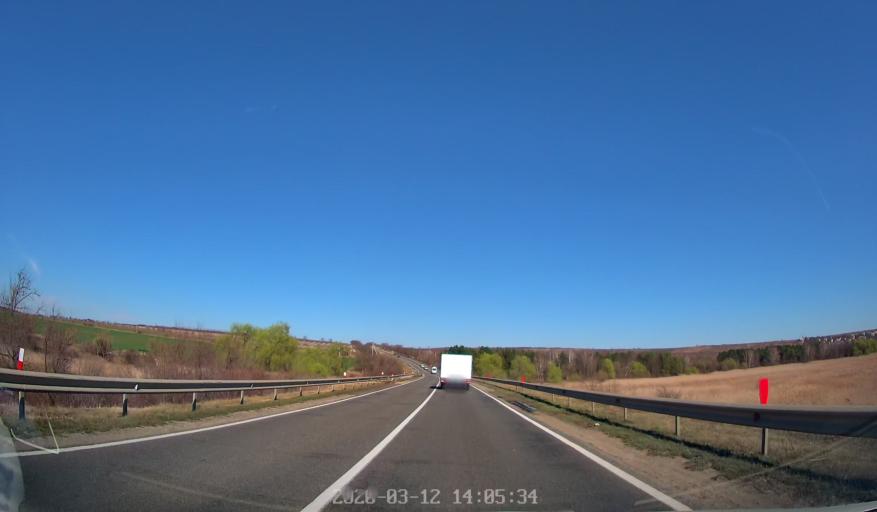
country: MD
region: Chisinau
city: Vatra
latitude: 46.9877
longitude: 28.6866
